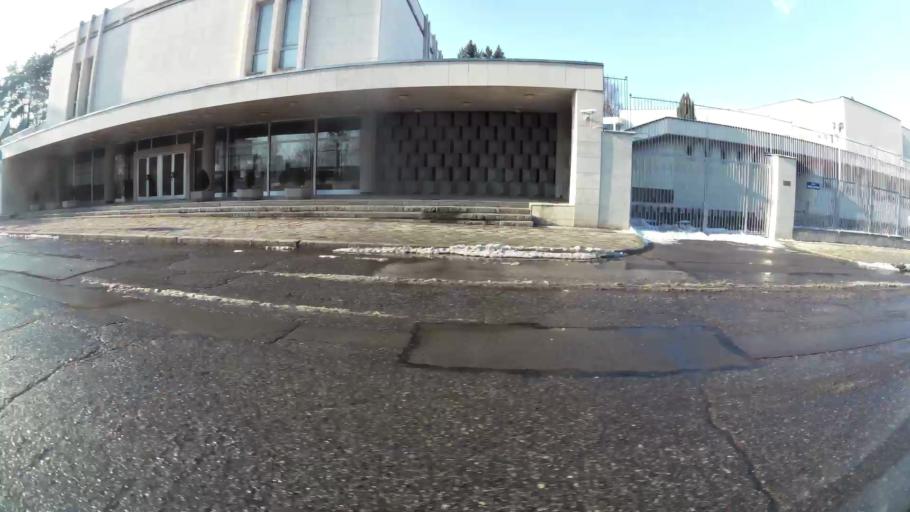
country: BG
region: Sofia-Capital
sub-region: Stolichna Obshtina
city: Sofia
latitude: 42.6717
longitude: 23.3466
